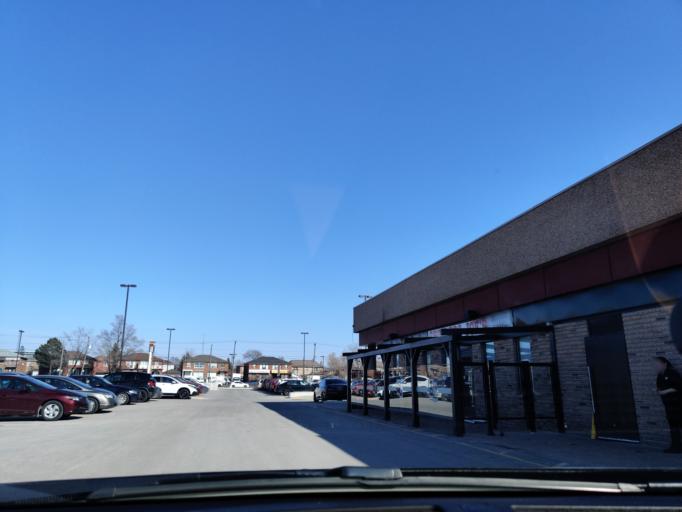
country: CA
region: Ontario
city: Toronto
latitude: 43.7192
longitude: -79.4575
